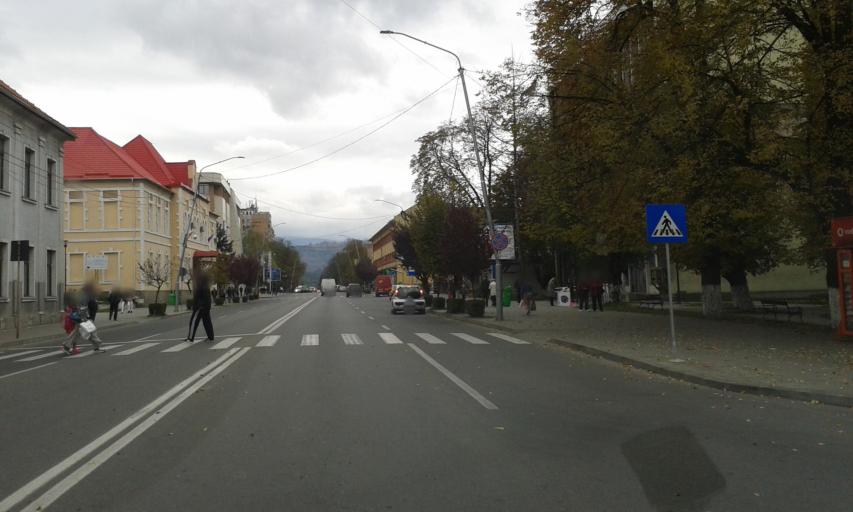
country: RO
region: Hunedoara
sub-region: Municipiul Petrosani
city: Petrosani
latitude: 45.4185
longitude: 23.3717
